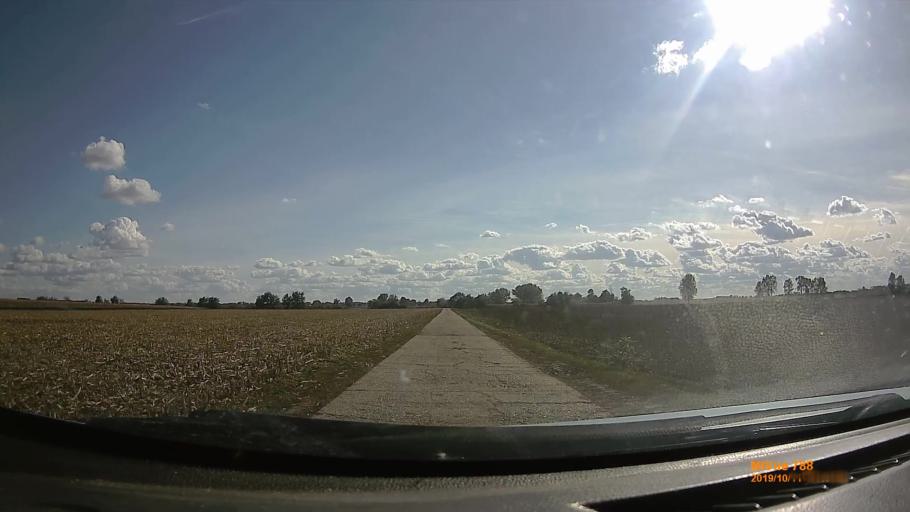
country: HU
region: Hajdu-Bihar
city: Hajduszoboszlo
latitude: 47.5332
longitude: 21.4015
